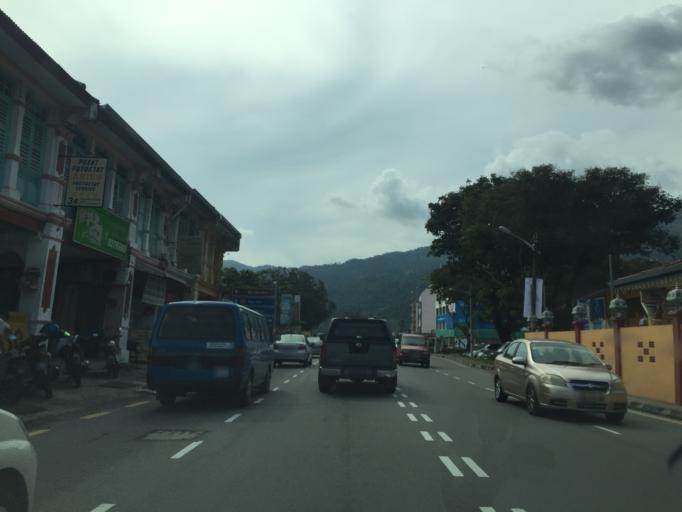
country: MY
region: Penang
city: George Town
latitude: 5.4046
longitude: 100.2896
